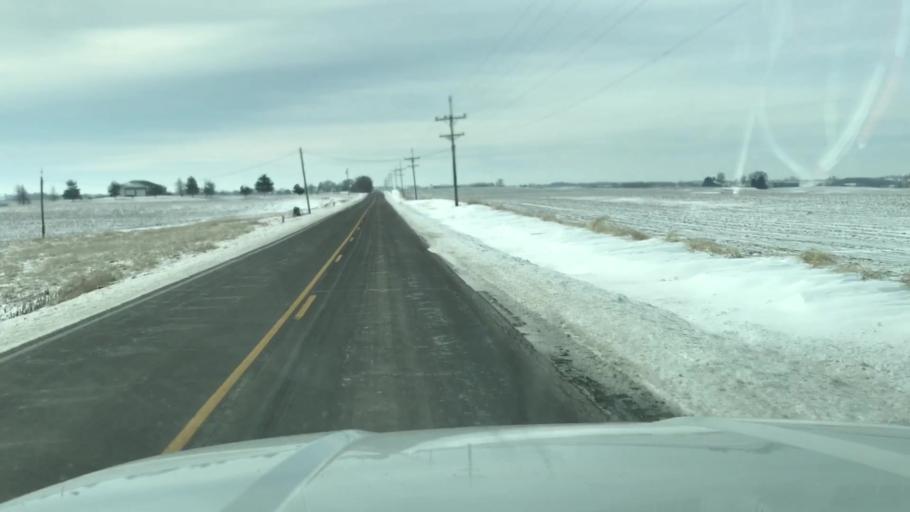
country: US
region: Missouri
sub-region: Holt County
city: Oregon
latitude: 40.0591
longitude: -95.1356
